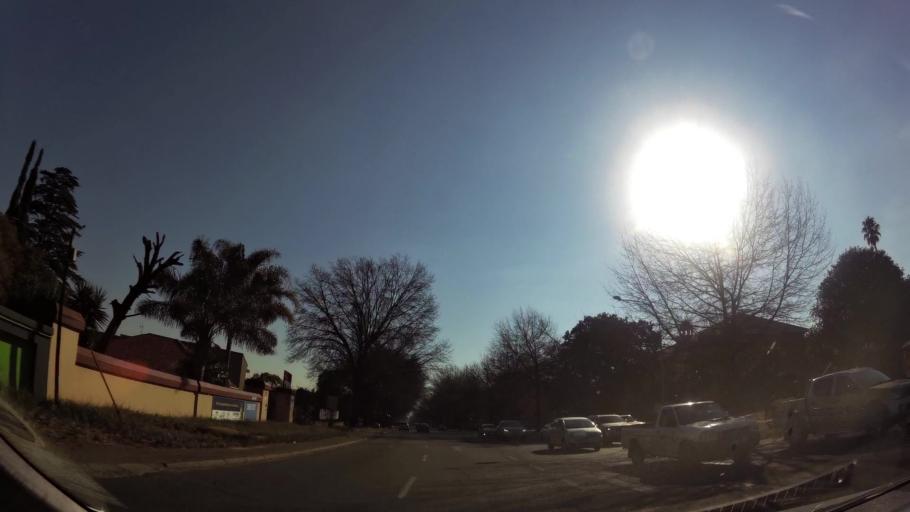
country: ZA
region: Gauteng
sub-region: Ekurhuleni Metropolitan Municipality
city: Germiston
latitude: -26.1873
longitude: 28.1359
